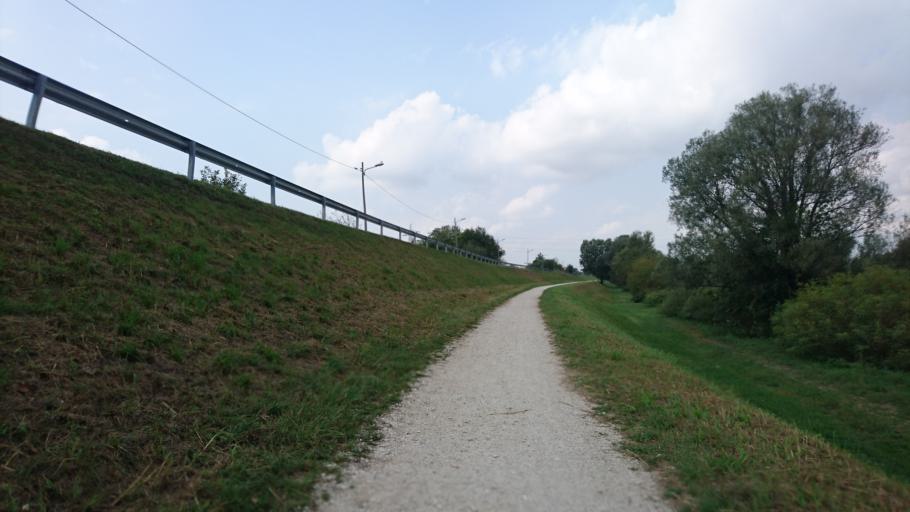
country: IT
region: Veneto
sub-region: Provincia di Padova
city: Mejaniga
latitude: 45.4397
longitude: 11.9078
